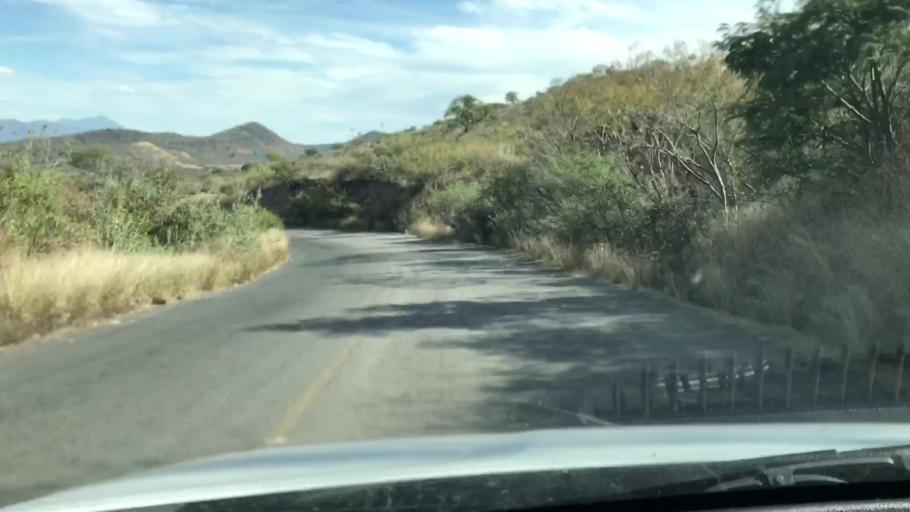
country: MX
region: Jalisco
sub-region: Zacoalco de Torres
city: Barranca de Otates (Barranca de Otatan)
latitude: 20.2565
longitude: -103.6725
